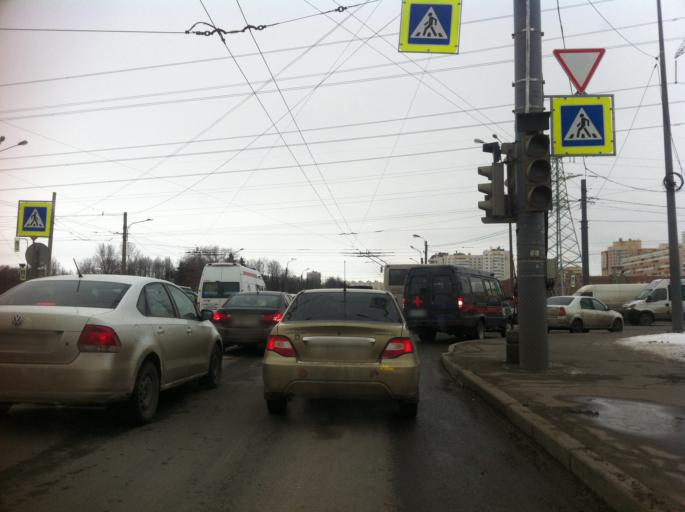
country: RU
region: St.-Petersburg
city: Uritsk
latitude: 59.8460
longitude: 30.1756
